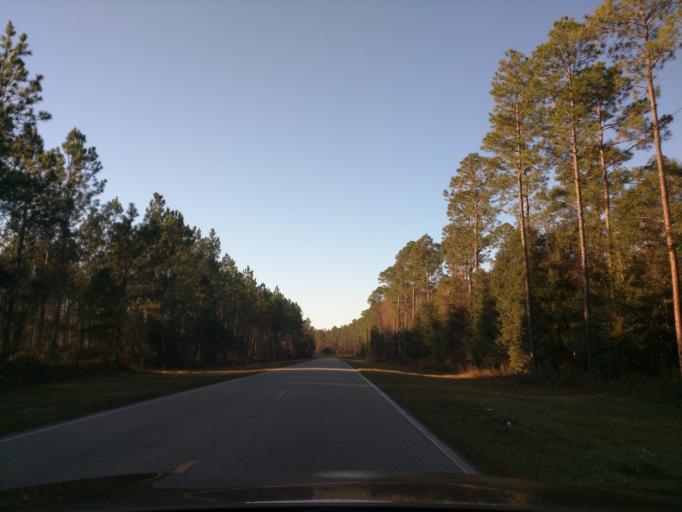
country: US
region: Florida
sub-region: Leon County
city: Woodville
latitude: 30.3578
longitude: -84.1306
